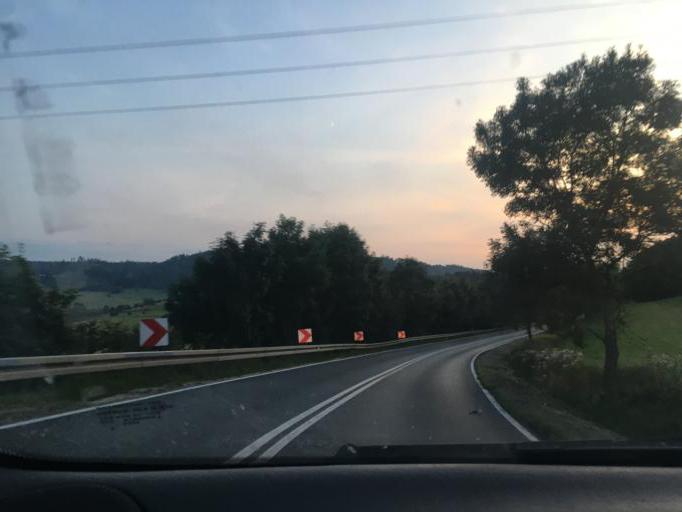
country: PL
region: Lower Silesian Voivodeship
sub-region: Powiat walbrzyski
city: Boguszow-Gorce
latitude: 50.7584
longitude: 16.1886
